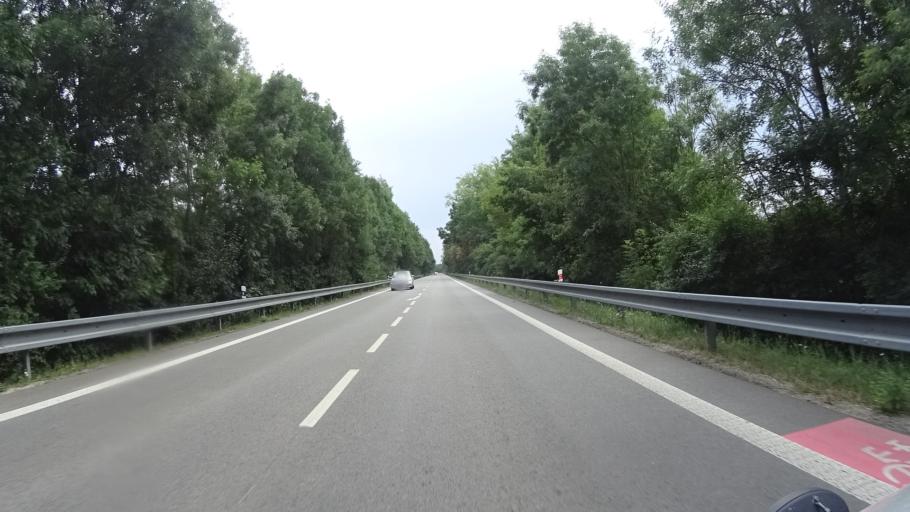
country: CZ
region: South Moravian
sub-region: Okres Breclav
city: Lednice
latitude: 48.8181
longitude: 16.8175
